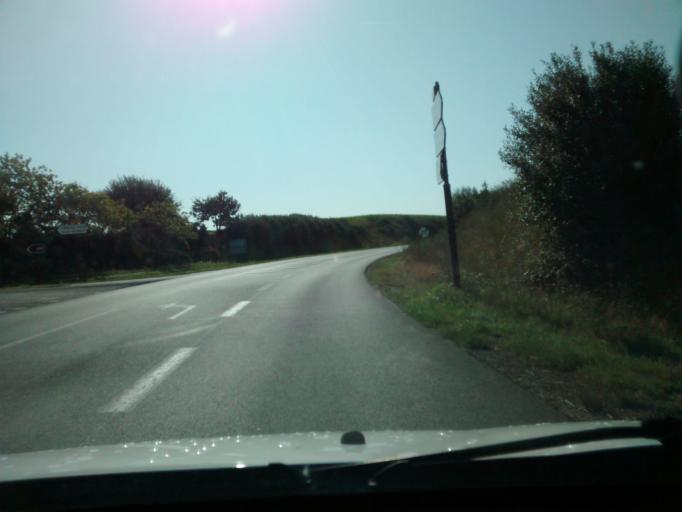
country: FR
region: Brittany
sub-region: Departement des Cotes-d'Armor
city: Penvenan
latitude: 48.7791
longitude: -3.3127
